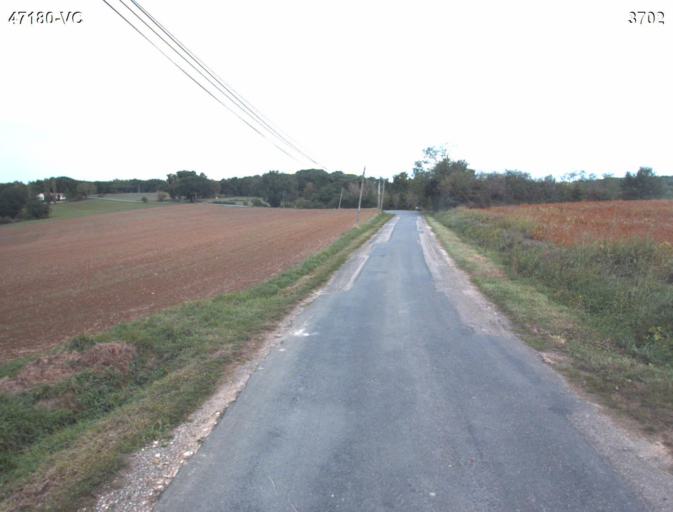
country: FR
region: Aquitaine
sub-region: Departement du Lot-et-Garonne
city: Sainte-Colombe-en-Bruilhois
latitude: 44.1648
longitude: 0.4571
